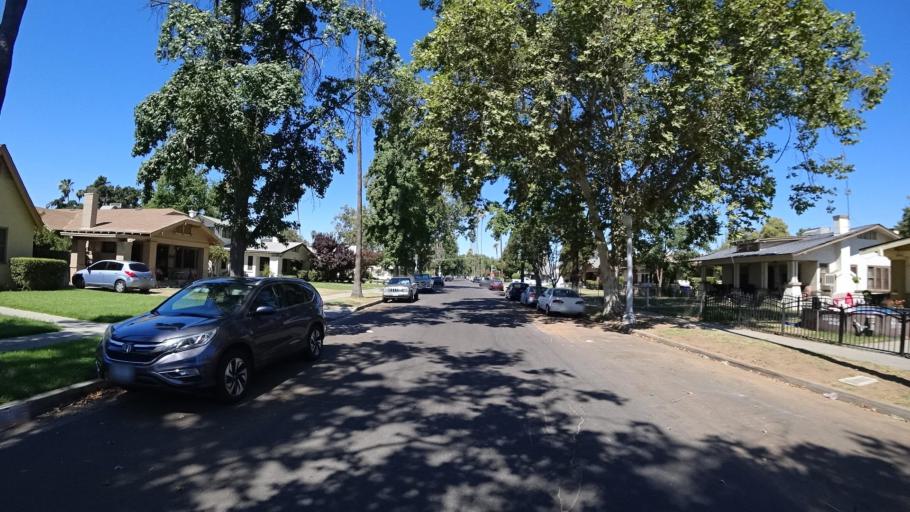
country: US
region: California
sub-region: Fresno County
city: Fresno
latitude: 36.7418
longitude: -119.7634
